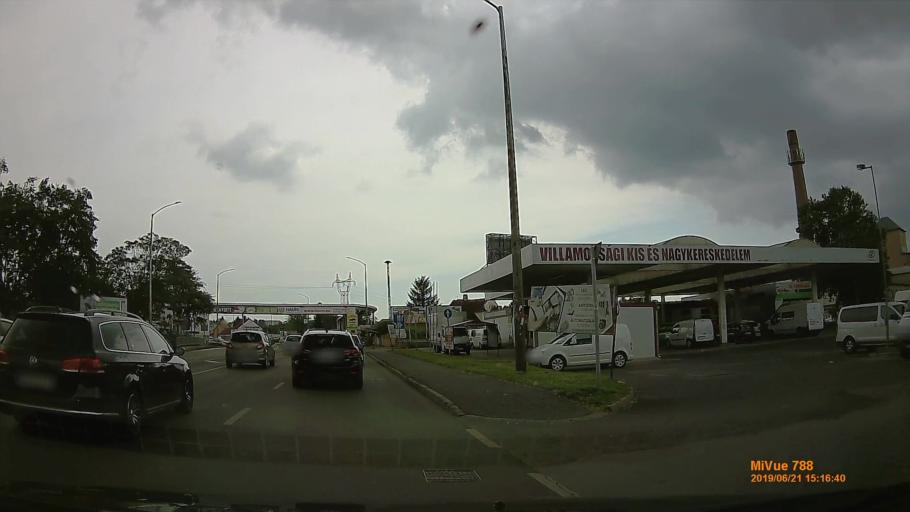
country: HU
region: Baranya
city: Pecs
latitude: 46.0622
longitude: 18.2310
